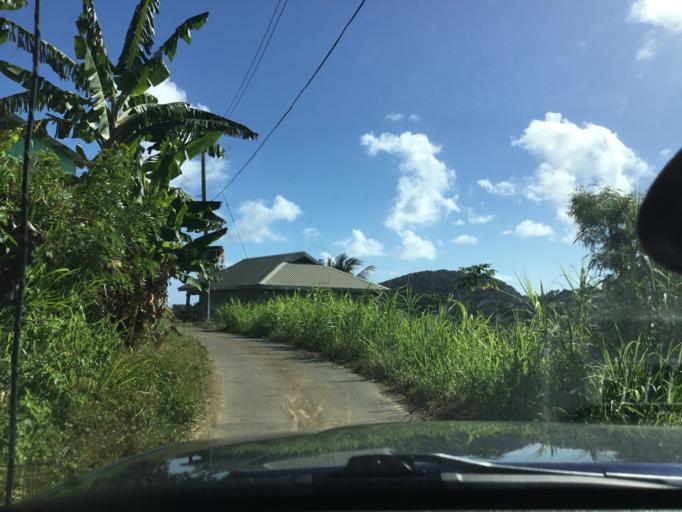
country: VC
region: Charlotte
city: Biabou
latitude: 13.1595
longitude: -61.1620
